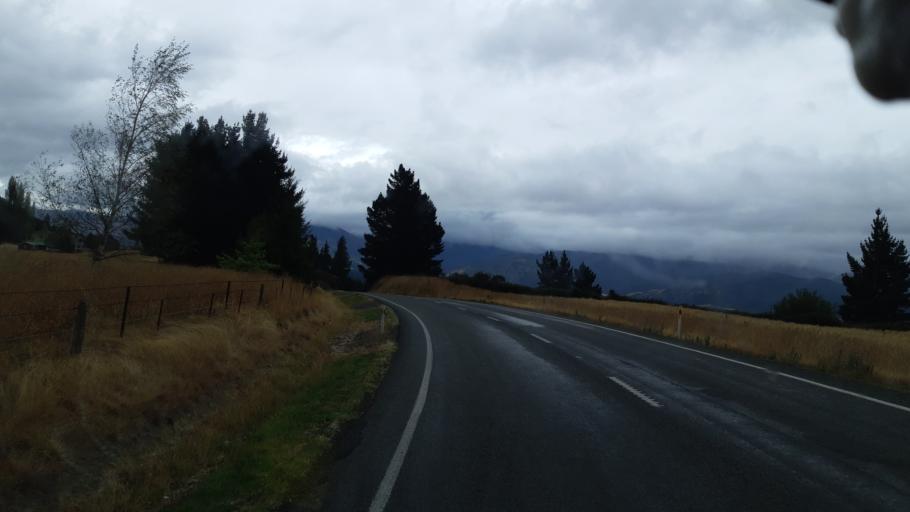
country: NZ
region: Canterbury
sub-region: Hurunui District
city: Amberley
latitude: -42.5831
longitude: 172.7765
